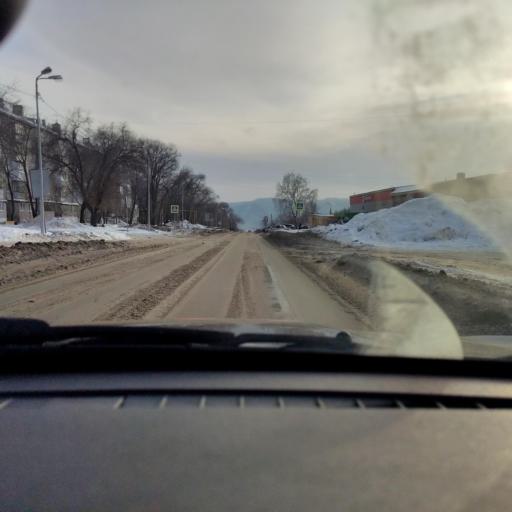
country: RU
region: Samara
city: Pribrezhnyy
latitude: 53.4882
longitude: 49.8468
